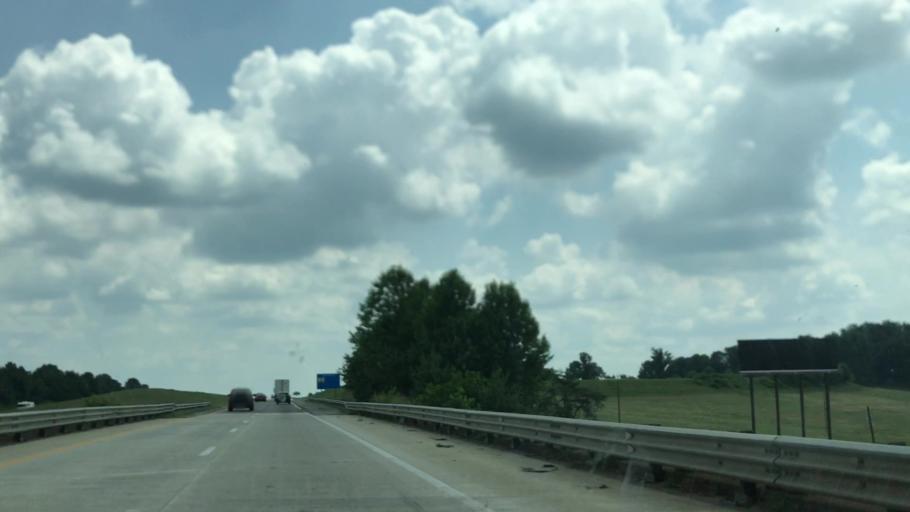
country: US
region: North Carolina
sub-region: Iredell County
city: Statesville
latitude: 35.9278
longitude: -80.8562
